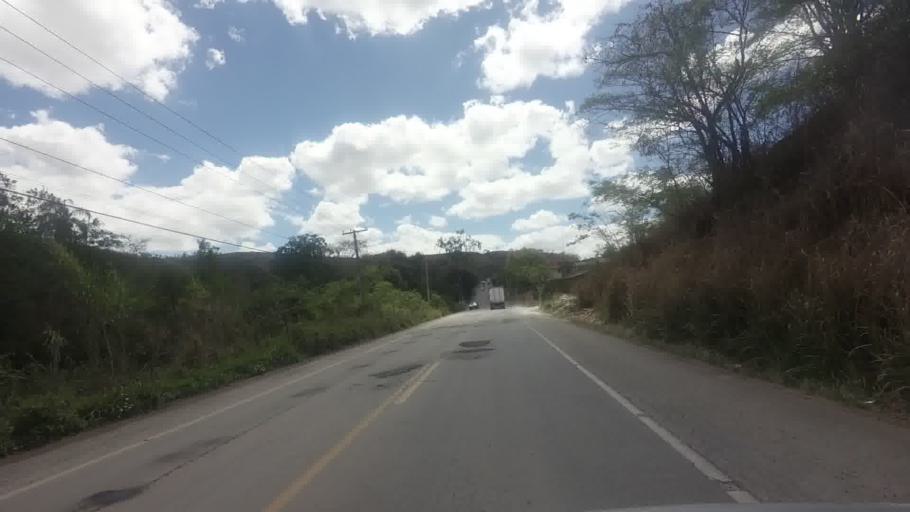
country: BR
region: Rio de Janeiro
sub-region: Santo Antonio De Padua
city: Santo Antonio de Padua
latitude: -21.6288
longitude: -42.2625
